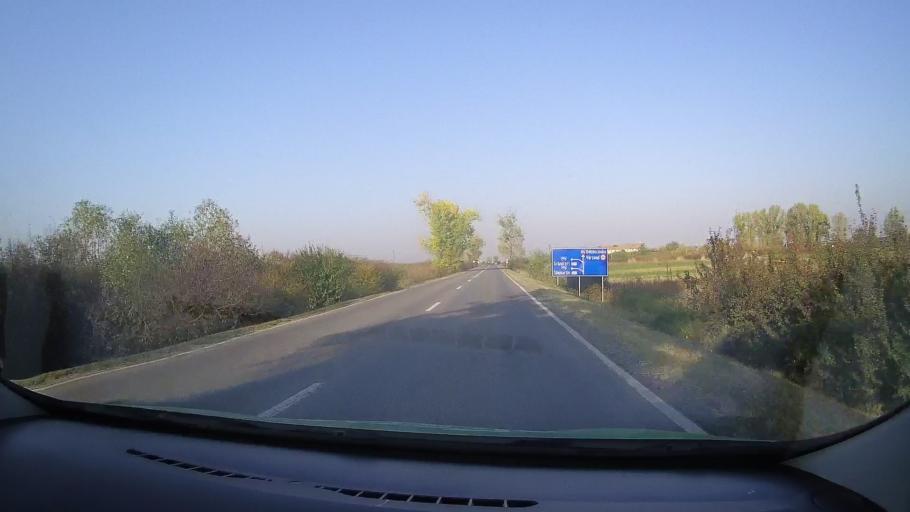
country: RO
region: Arad
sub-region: Comuna Socodor
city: Socodor
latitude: 46.5018
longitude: 21.4273
